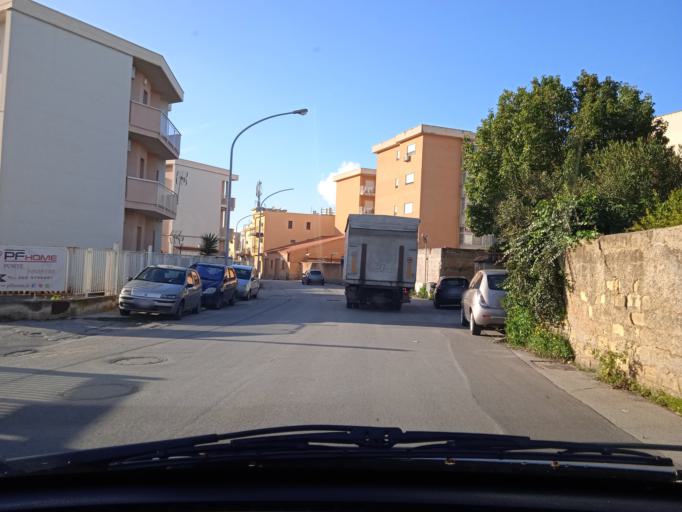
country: IT
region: Sicily
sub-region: Palermo
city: Ciaculli
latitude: 38.0871
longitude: 13.4223
